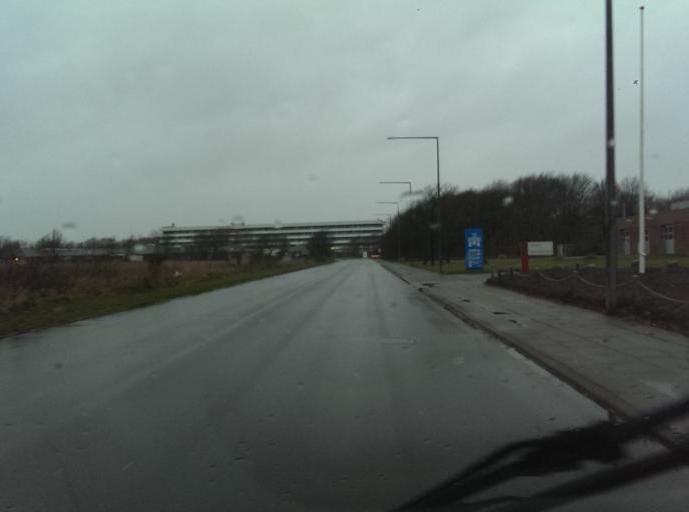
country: DK
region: South Denmark
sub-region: Esbjerg Kommune
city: Esbjerg
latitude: 55.4863
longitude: 8.4953
